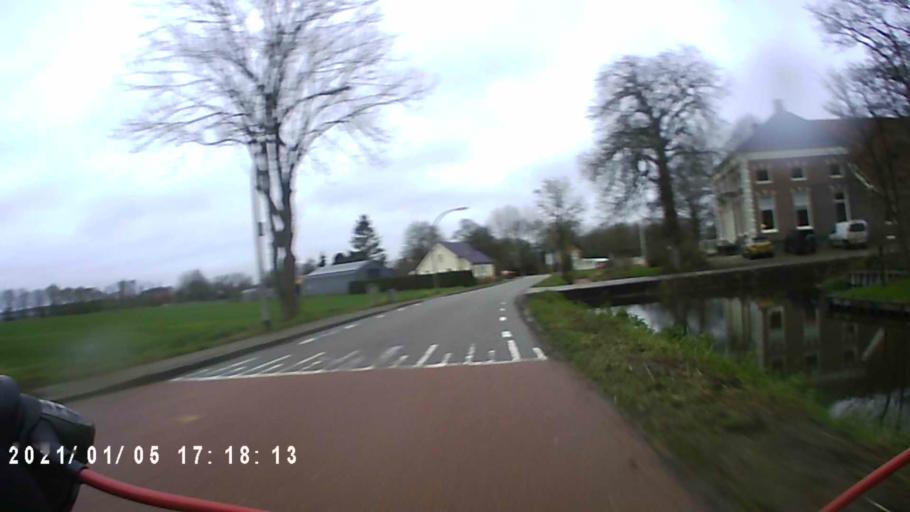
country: NL
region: Groningen
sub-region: Gemeente Delfzijl
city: Delfzijl
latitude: 53.2410
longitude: 6.9667
